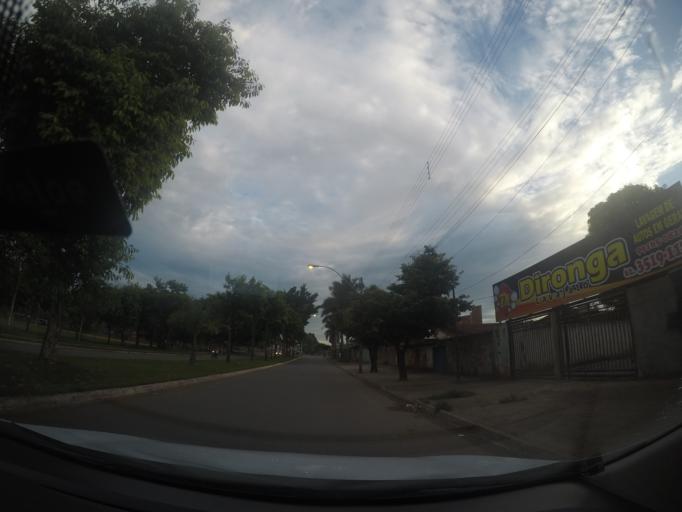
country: BR
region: Goias
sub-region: Goiania
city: Goiania
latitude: -16.6918
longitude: -49.3508
